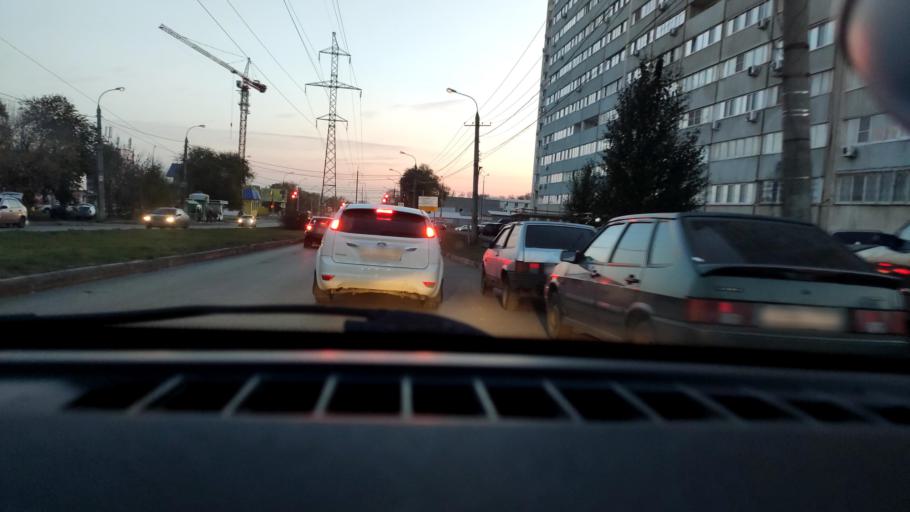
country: RU
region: Samara
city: Samara
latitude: 53.2078
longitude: 50.2134
